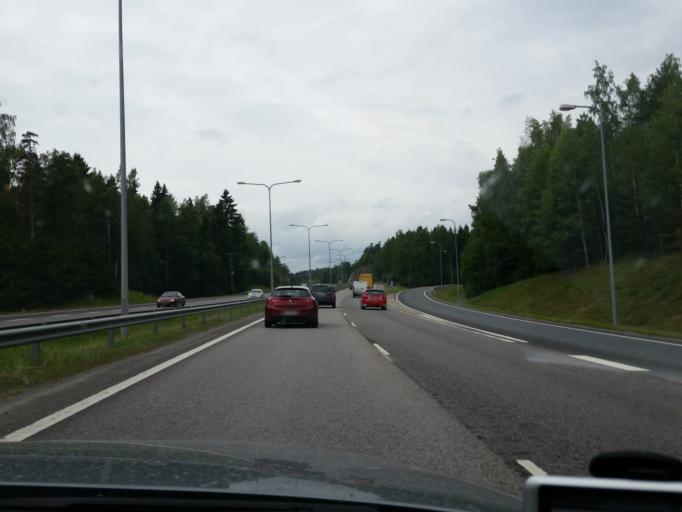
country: FI
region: Uusimaa
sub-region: Helsinki
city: Kauniainen
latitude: 60.2032
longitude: 24.7007
